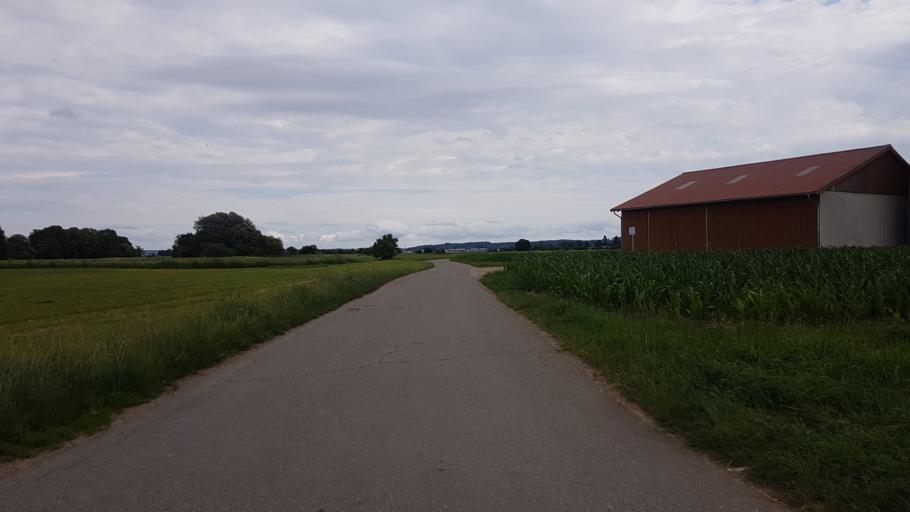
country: DE
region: Baden-Wuerttemberg
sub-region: Tuebingen Region
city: Mengen
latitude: 48.0619
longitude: 9.3506
